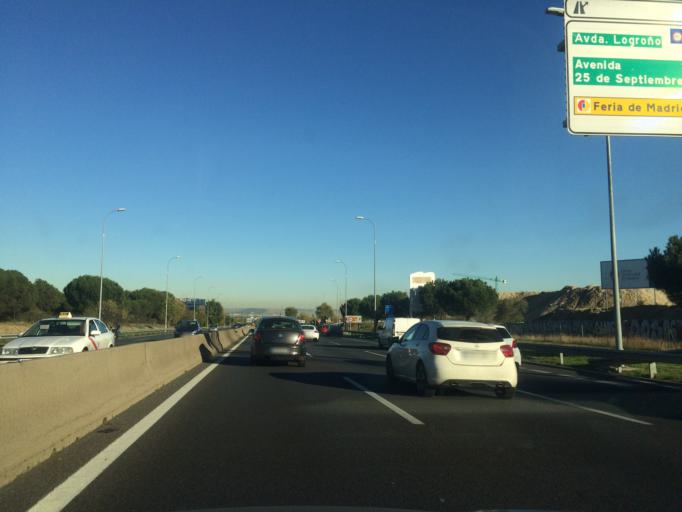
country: ES
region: Madrid
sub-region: Provincia de Madrid
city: San Blas
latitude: 40.4496
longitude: -3.6240
